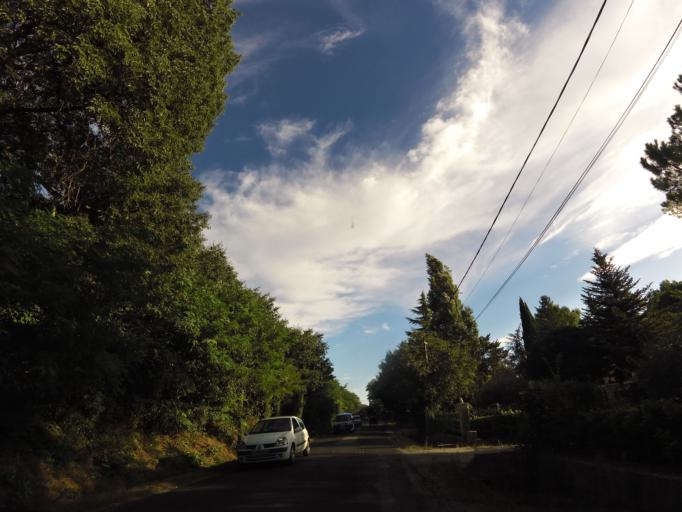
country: FR
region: Languedoc-Roussillon
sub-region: Departement du Gard
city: Sommieres
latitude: 43.7744
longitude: 4.0925
